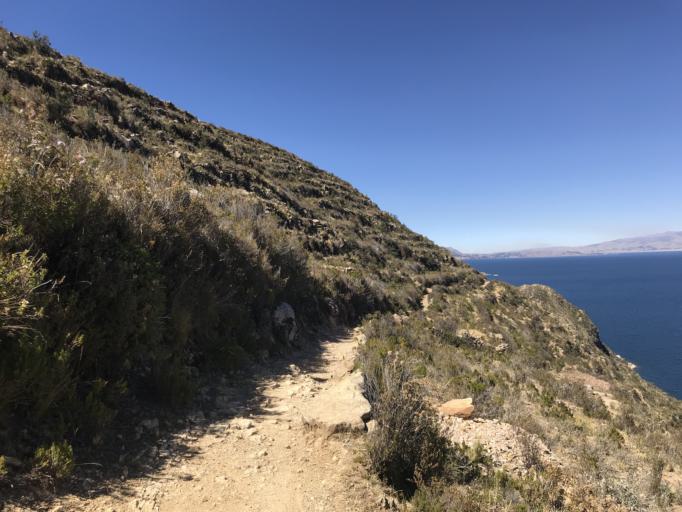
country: BO
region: La Paz
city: Yumani
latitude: -16.0411
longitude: -69.1483
